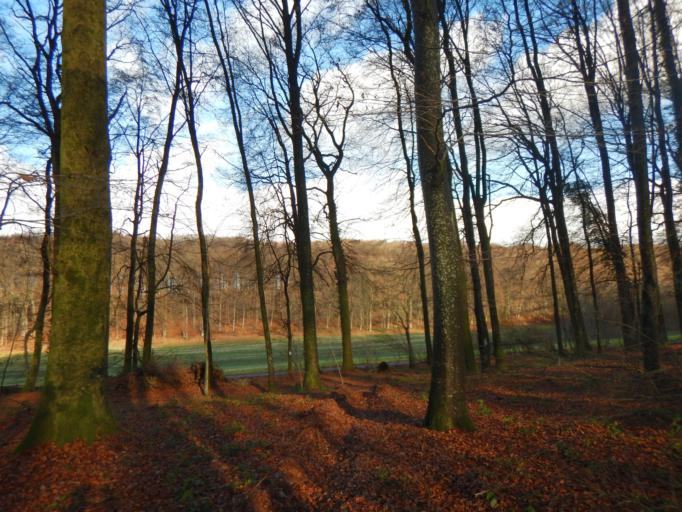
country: LU
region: Diekirch
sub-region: Canton de Redange
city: Redange-sur-Attert
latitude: 49.7741
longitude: 5.9120
